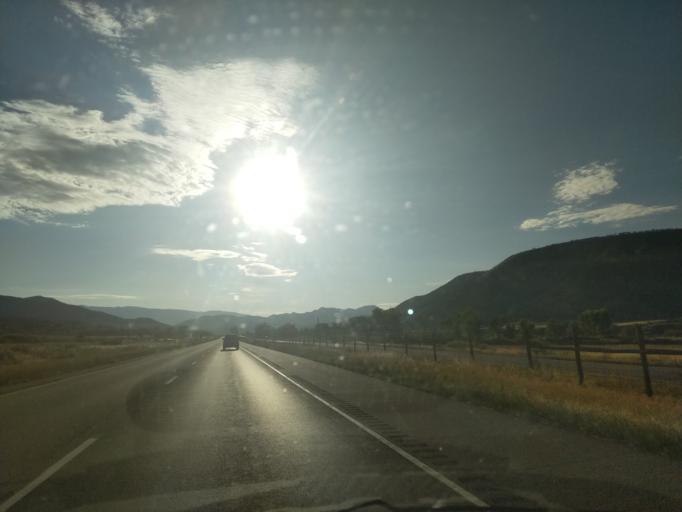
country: US
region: Colorado
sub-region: Garfield County
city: Silt
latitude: 39.5486
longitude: -107.6091
